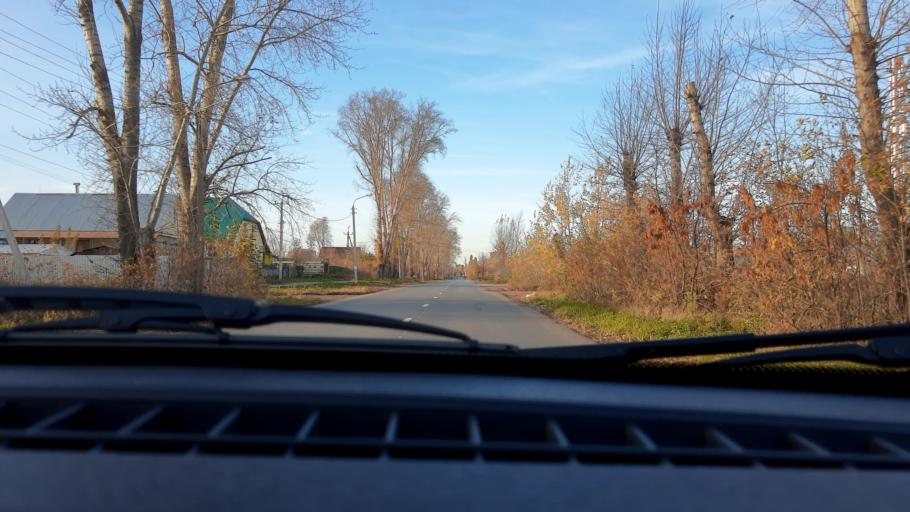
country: RU
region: Bashkortostan
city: Mikhaylovka
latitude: 54.7699
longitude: 55.8954
